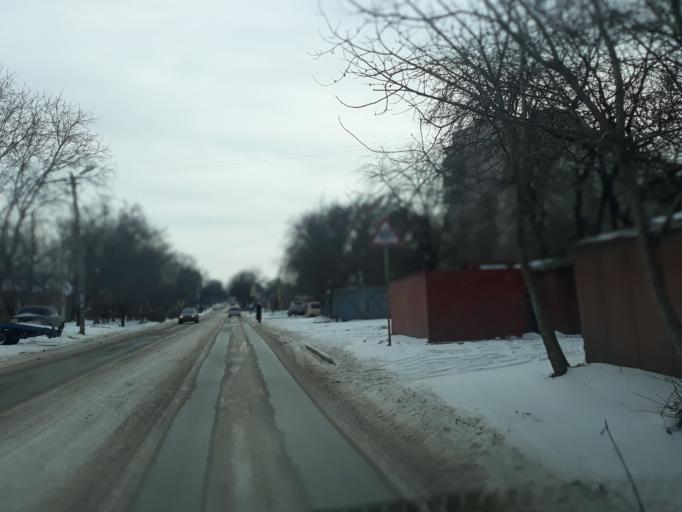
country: RU
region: Rostov
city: Taganrog
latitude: 47.2269
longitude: 38.8762
